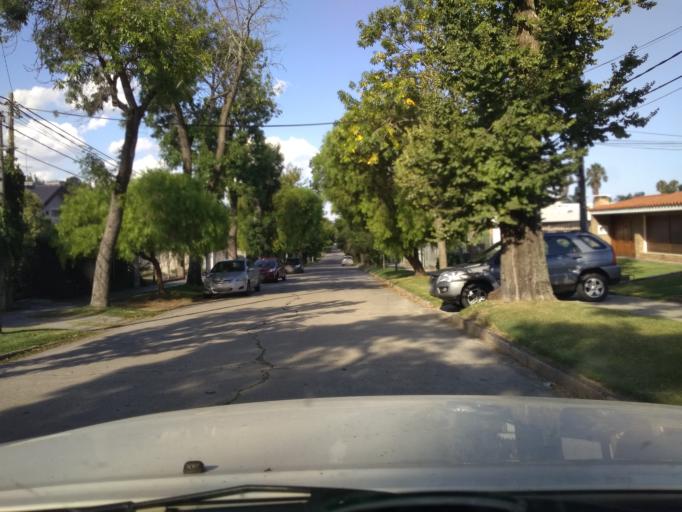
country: UY
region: Canelones
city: Paso de Carrasco
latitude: -34.8880
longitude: -56.0779
